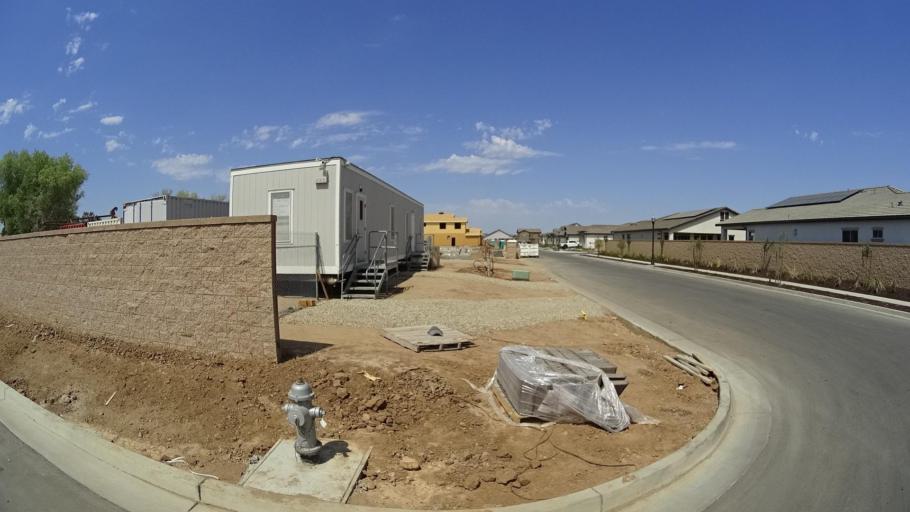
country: US
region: California
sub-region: Fresno County
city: Tarpey Village
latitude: 36.7742
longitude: -119.6753
